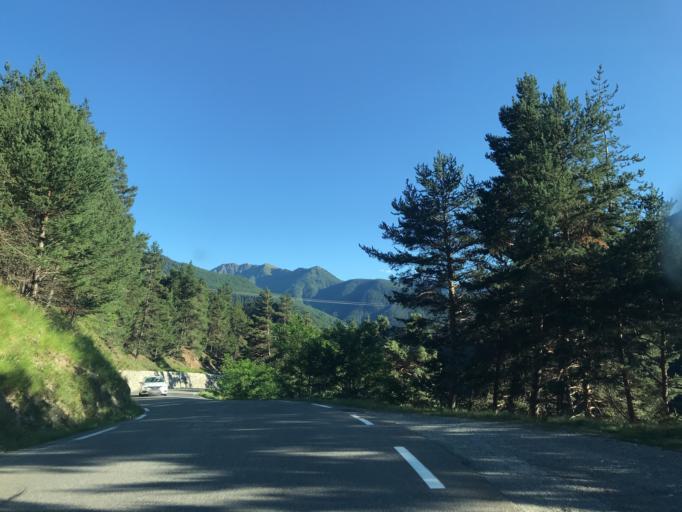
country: FR
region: Provence-Alpes-Cote d'Azur
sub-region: Departement des Hautes-Alpes
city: Guillestre
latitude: 44.7497
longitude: 6.7663
